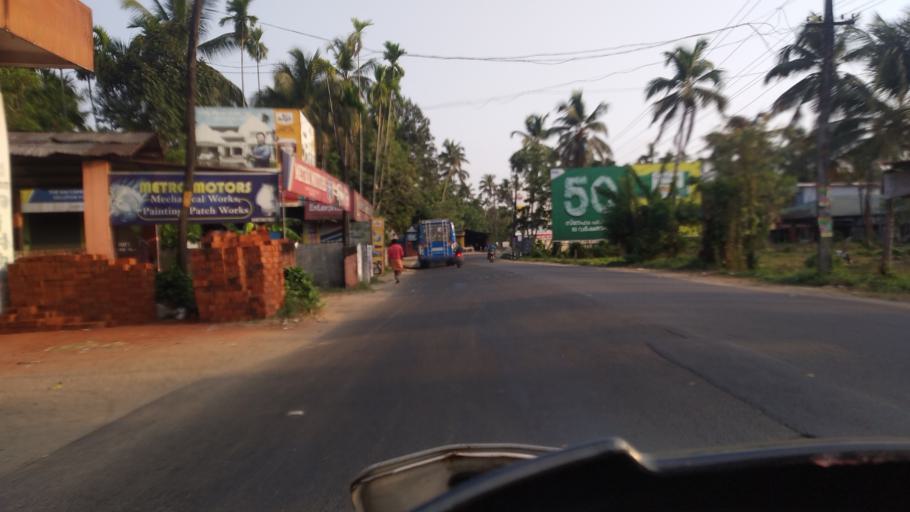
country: IN
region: Kerala
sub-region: Thrissur District
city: Thanniyam
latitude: 10.3689
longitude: 76.1249
